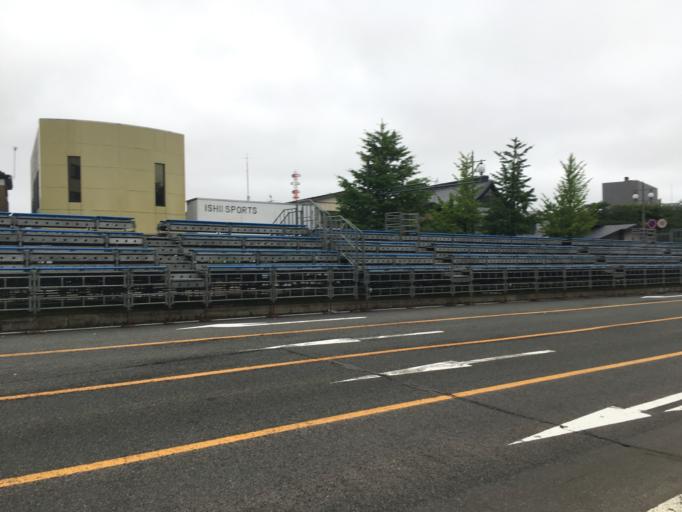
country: JP
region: Akita
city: Akita
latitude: 39.7188
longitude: 140.1122
